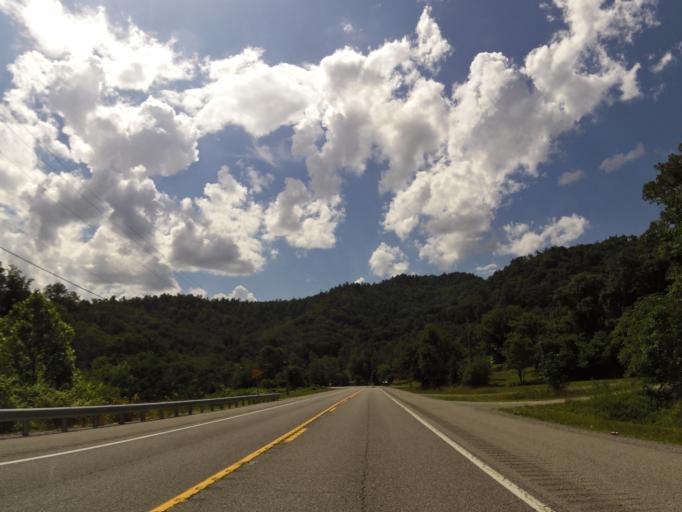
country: US
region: Kentucky
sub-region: Harlan County
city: Harlan
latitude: 36.8144
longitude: -83.2837
